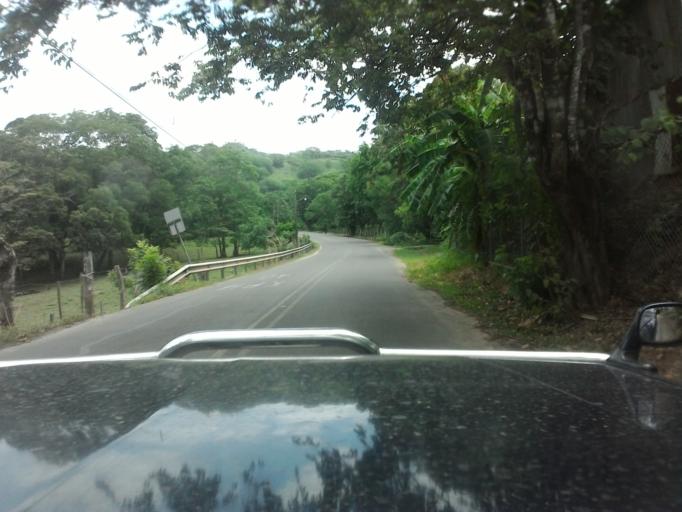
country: CR
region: Guanacaste
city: Juntas
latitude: 10.2107
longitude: -84.8492
